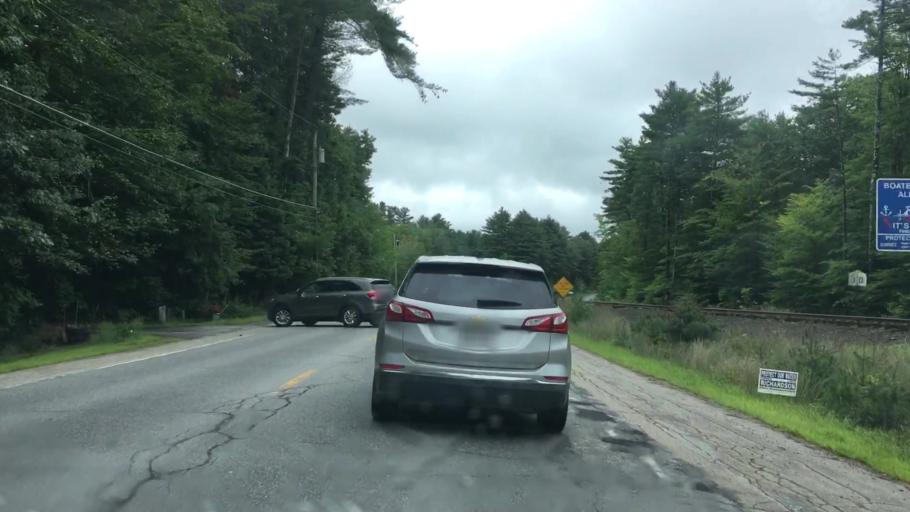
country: US
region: Maine
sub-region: Oxford County
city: Fryeburg
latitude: 44.0062
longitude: -70.9912
